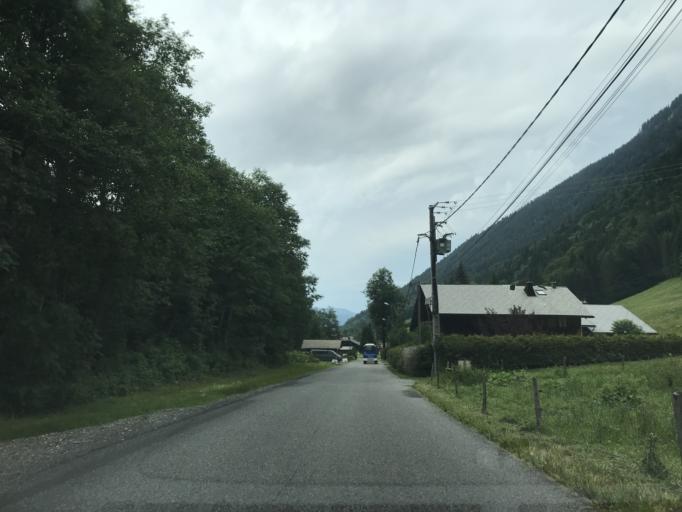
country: FR
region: Rhone-Alpes
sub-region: Departement de la Haute-Savoie
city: Morzine
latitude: 46.1547
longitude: 6.7358
